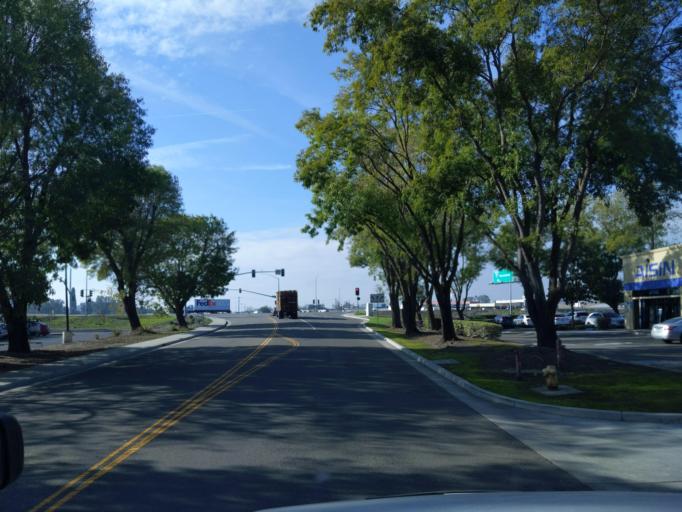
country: US
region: California
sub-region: San Joaquin County
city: French Camp
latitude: 37.8972
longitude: -121.2786
